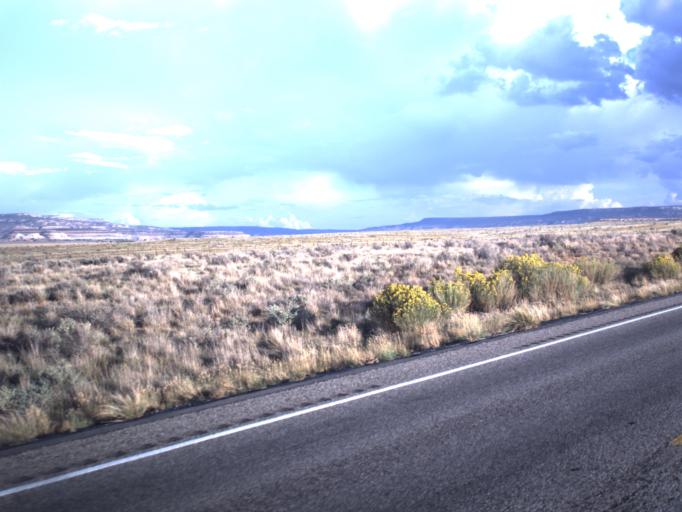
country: US
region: Utah
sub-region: San Juan County
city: Monticello
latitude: 38.1581
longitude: -109.3759
